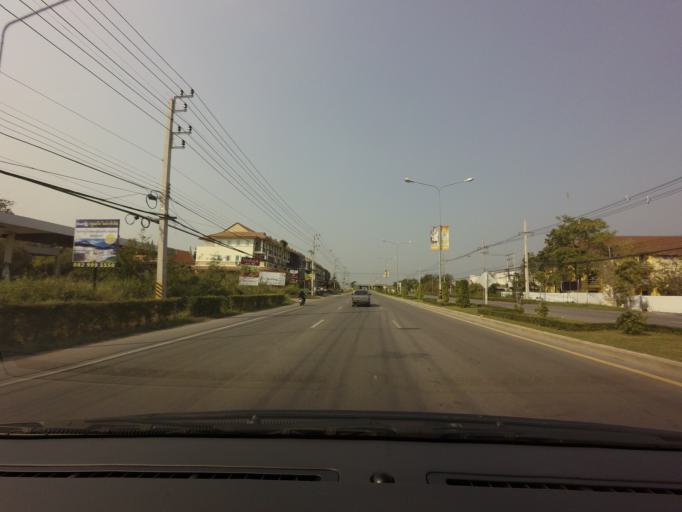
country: TH
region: Prachuap Khiri Khan
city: Hua Hin
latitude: 12.6378
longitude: 99.9484
